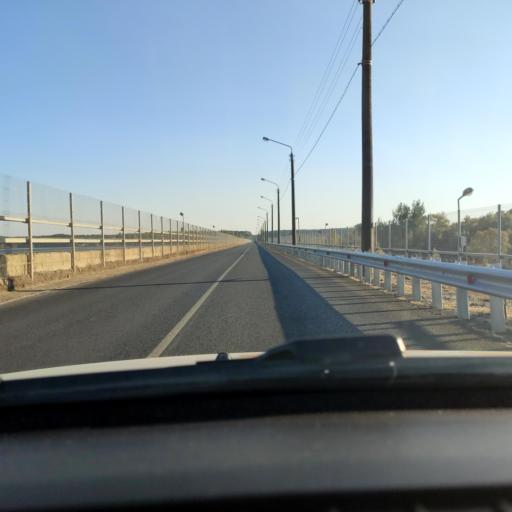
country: RU
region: Voronezj
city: Shilovo
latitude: 51.5460
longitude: 39.1361
